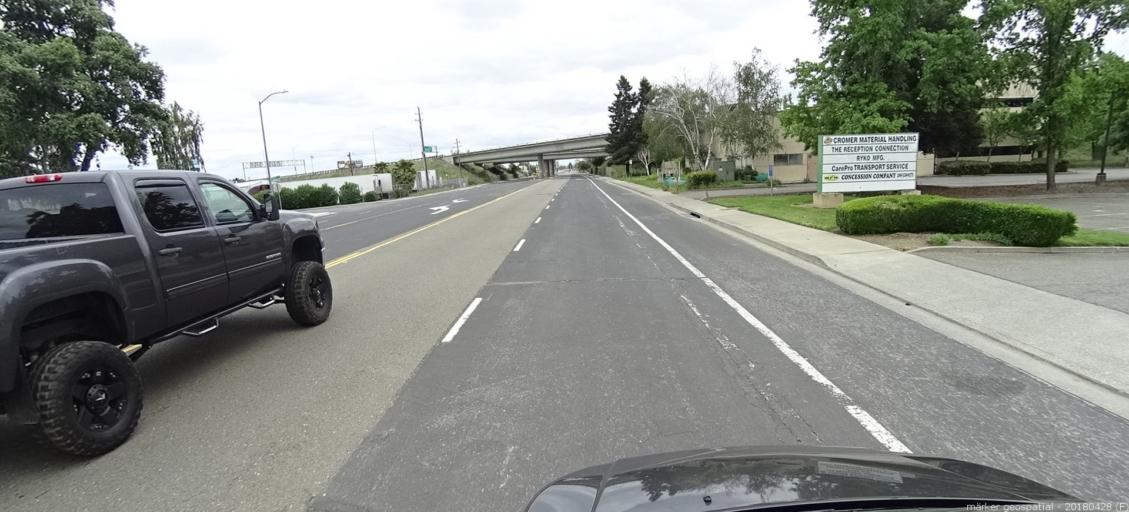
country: US
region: California
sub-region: Yolo County
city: West Sacramento
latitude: 38.5784
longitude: -121.5632
